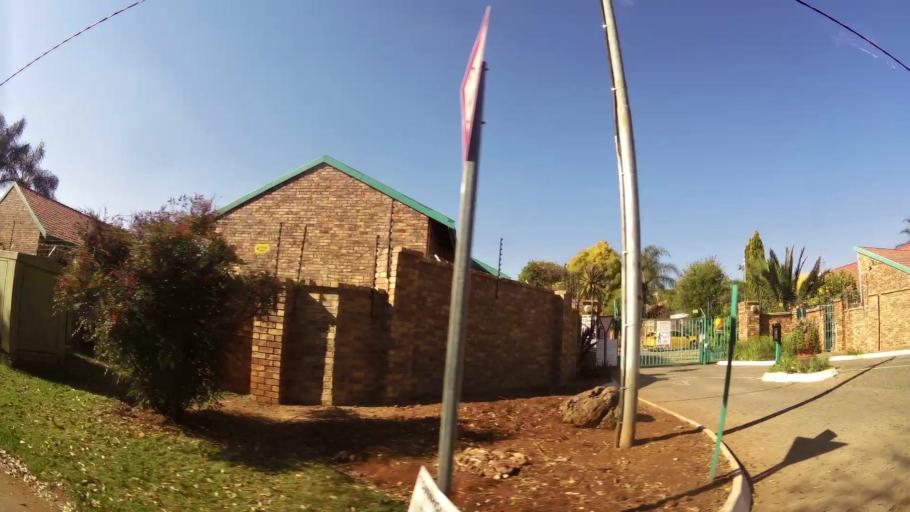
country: ZA
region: Gauteng
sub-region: City of Tshwane Metropolitan Municipality
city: Centurion
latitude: -25.8372
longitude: 28.1782
